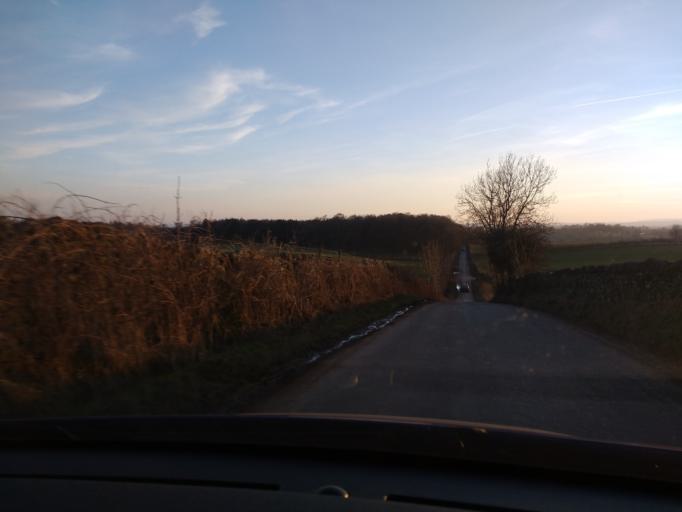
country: GB
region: England
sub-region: Cumbria
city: Appleby-in-Westmorland
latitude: 54.6088
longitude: -2.4841
